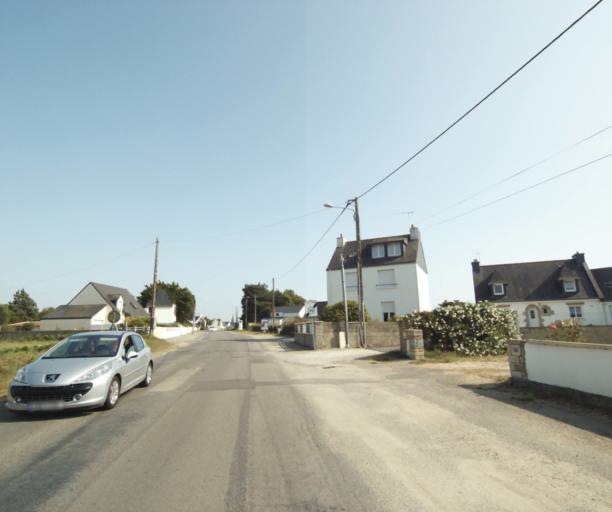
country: FR
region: Brittany
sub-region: Departement du Morbihan
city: Merlevenez
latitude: 47.7023
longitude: -3.2598
